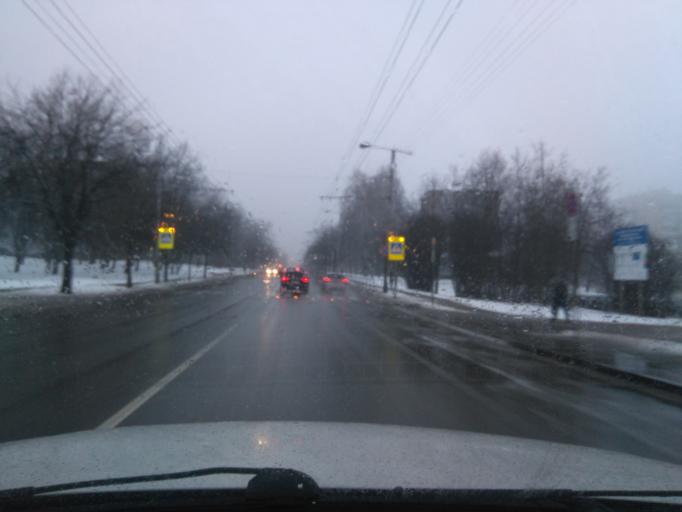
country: LT
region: Kauno apskritis
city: Dainava (Kaunas)
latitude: 54.9071
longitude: 23.9738
